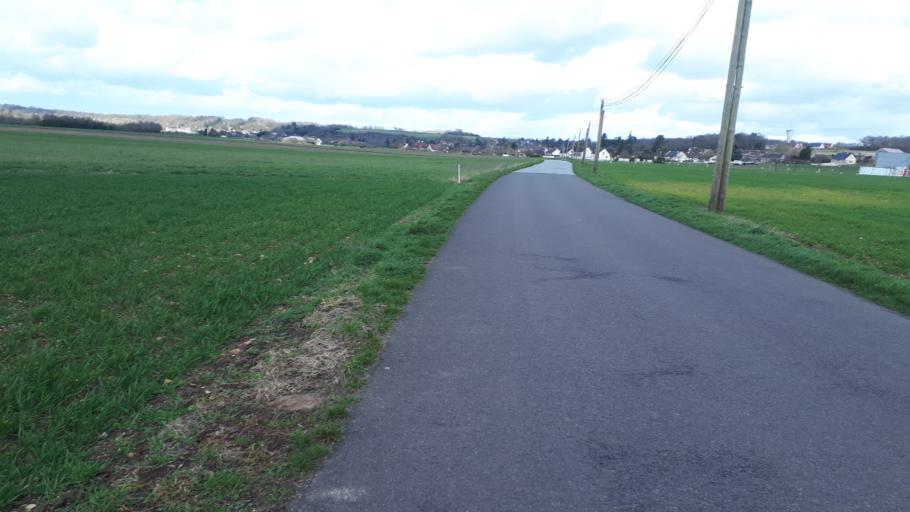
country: FR
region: Centre
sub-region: Departement du Loir-et-Cher
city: Villiers-sur-Loir
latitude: 47.7964
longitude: 1.0002
